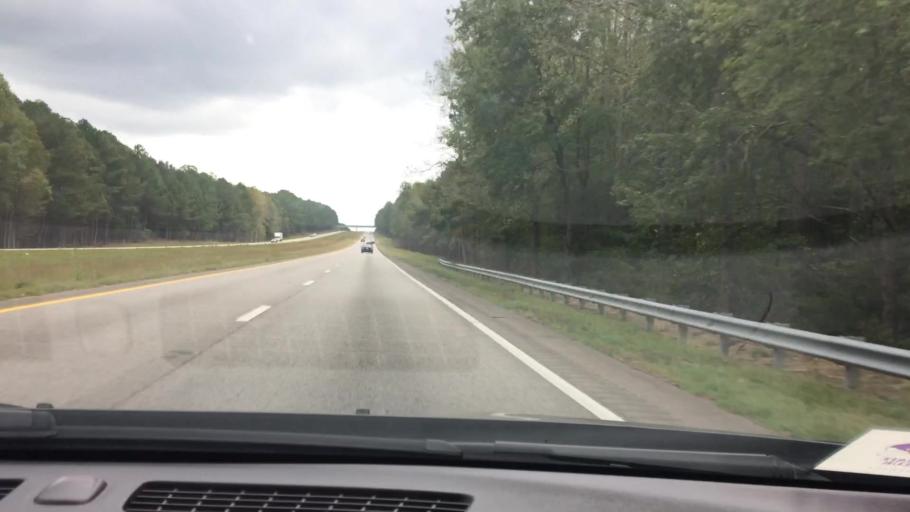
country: US
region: North Carolina
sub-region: Wake County
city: Zebulon
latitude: 35.8129
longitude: -78.2352
